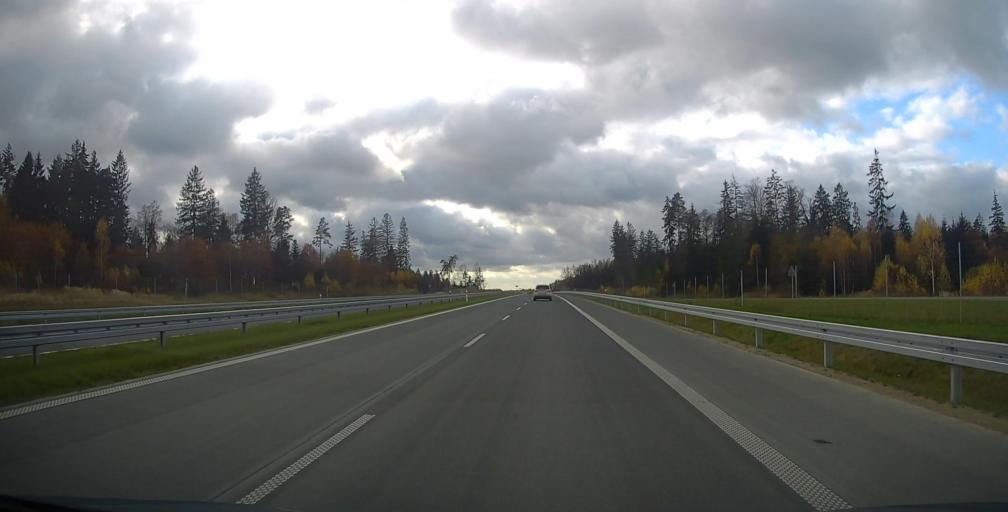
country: PL
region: Podlasie
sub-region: Powiat suwalski
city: Raczki
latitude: 53.8991
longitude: 22.6914
